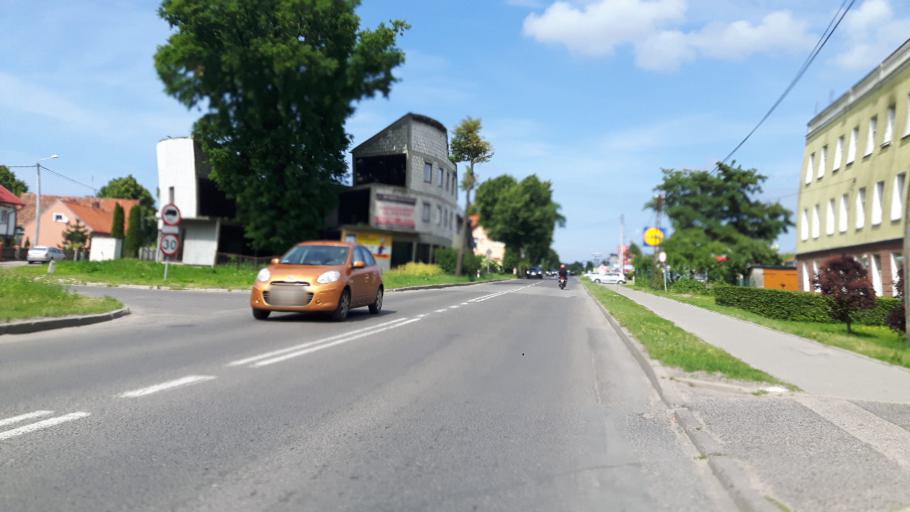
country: PL
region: Warmian-Masurian Voivodeship
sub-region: Powiat braniewski
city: Braniewo
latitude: 54.3884
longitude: 19.8328
